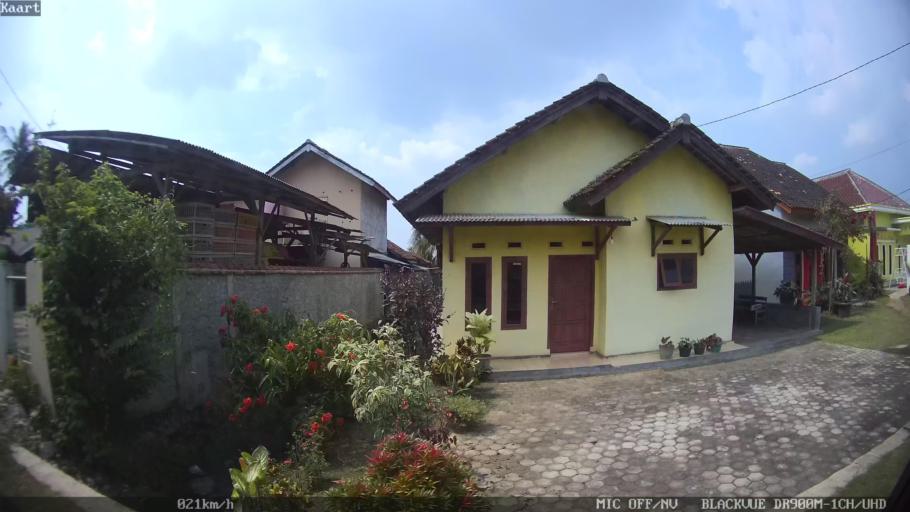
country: ID
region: Lampung
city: Gadingrejo
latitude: -5.3652
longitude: 105.0633
